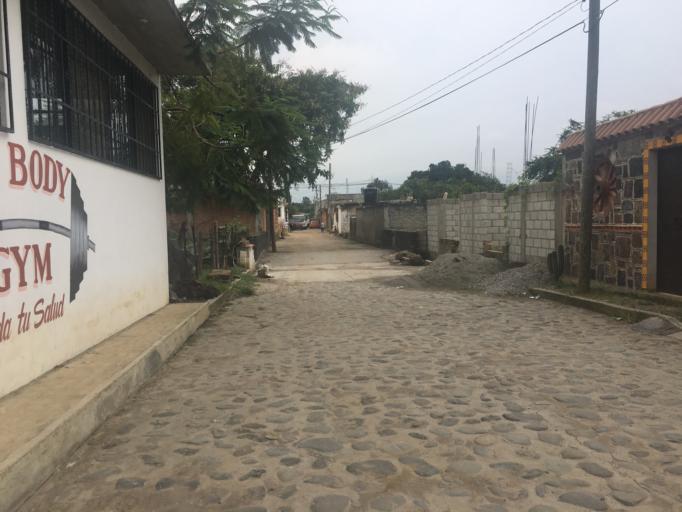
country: MX
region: Morelos
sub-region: Tlayacapan
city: Tlayacapan
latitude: 18.9614
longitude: -98.9837
